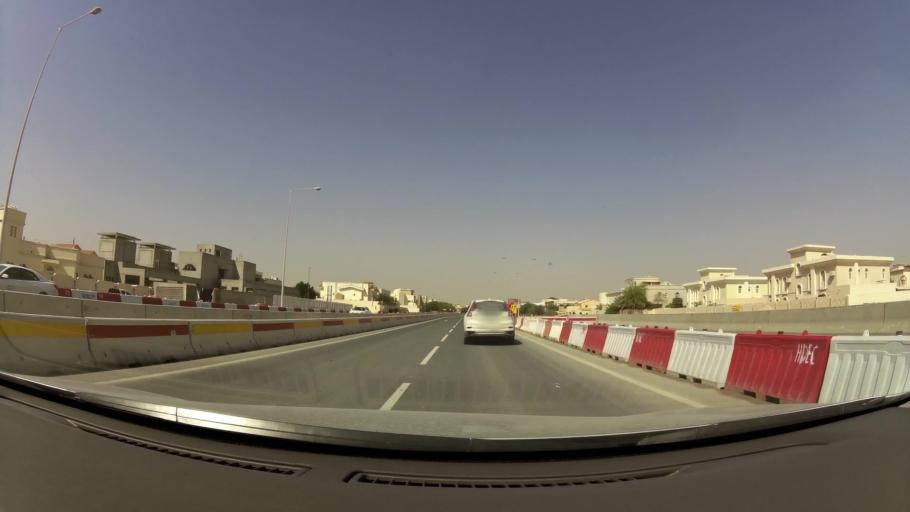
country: QA
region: Baladiyat ad Dawhah
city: Doha
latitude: 25.3525
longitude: 51.5096
